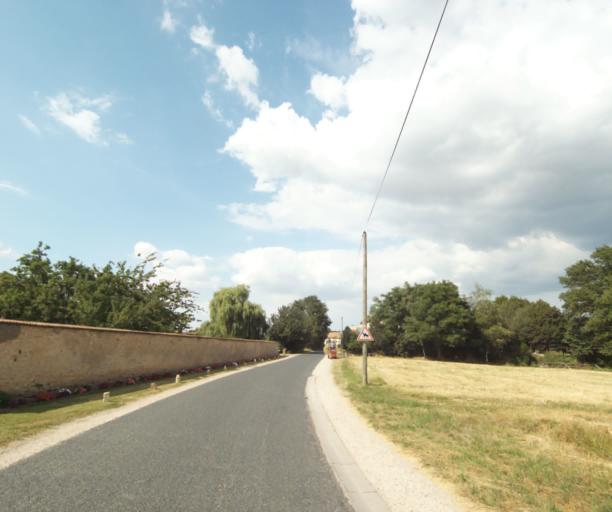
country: FR
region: Lorraine
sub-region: Departement de Meurthe-et-Moselle
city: Chanteheux
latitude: 48.5792
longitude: 6.5369
